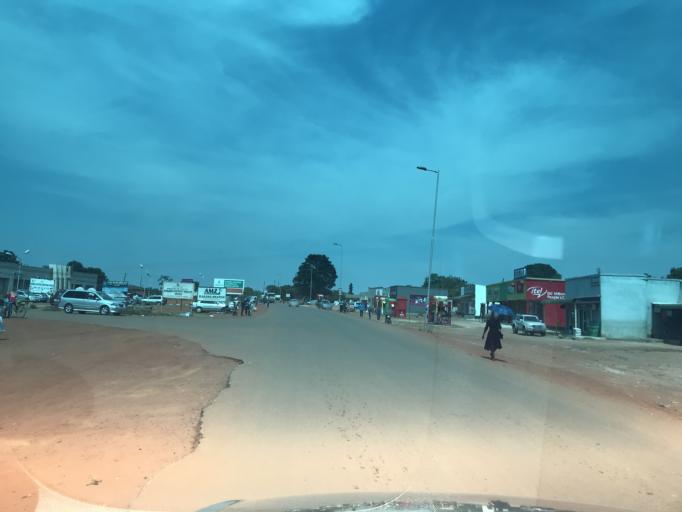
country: ZM
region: Northern
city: Kasama
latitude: -10.2051
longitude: 31.1834
